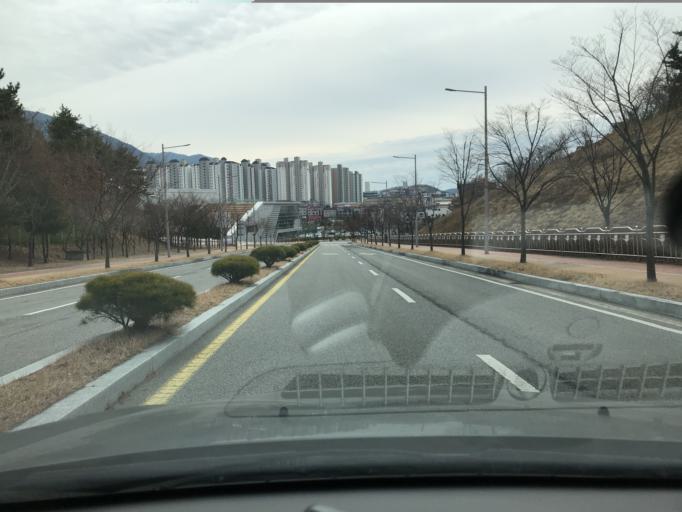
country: KR
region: Daegu
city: Hwawon
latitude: 35.7028
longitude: 128.4580
